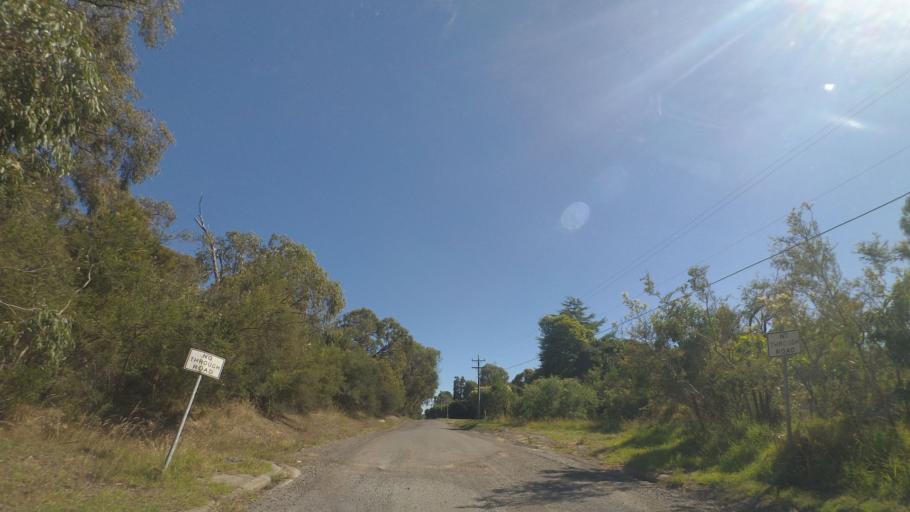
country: AU
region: Victoria
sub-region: Knox
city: Wantirna South
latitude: -37.8762
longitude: 145.2000
